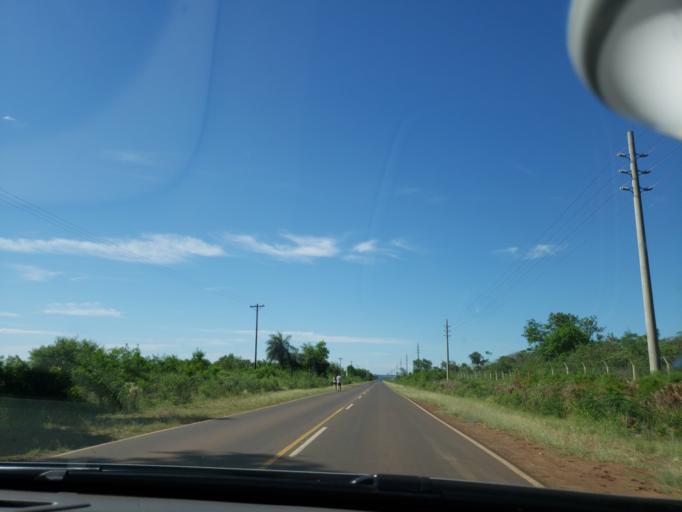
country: AR
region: Misiones
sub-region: Departamento de Capital
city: Posadas
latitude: -27.3960
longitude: -55.9762
